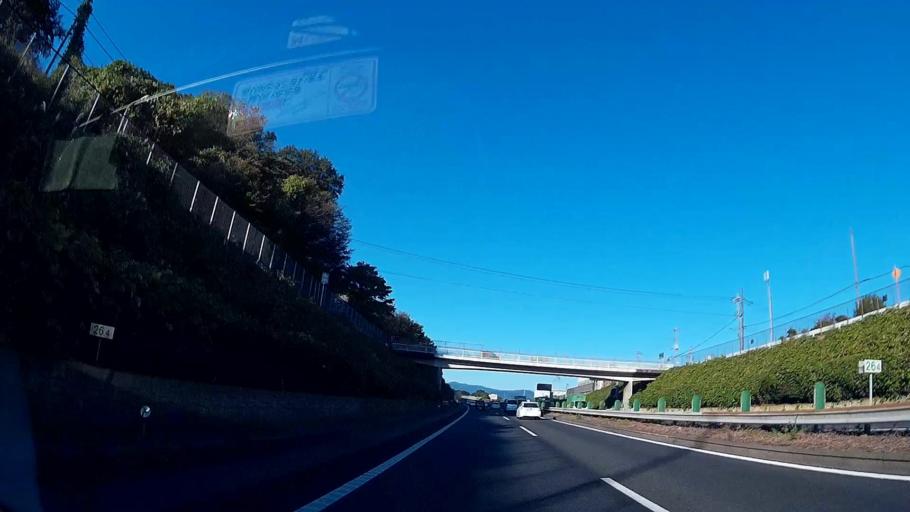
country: JP
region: Tokyo
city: Hachioji
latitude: 35.6770
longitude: 139.3424
